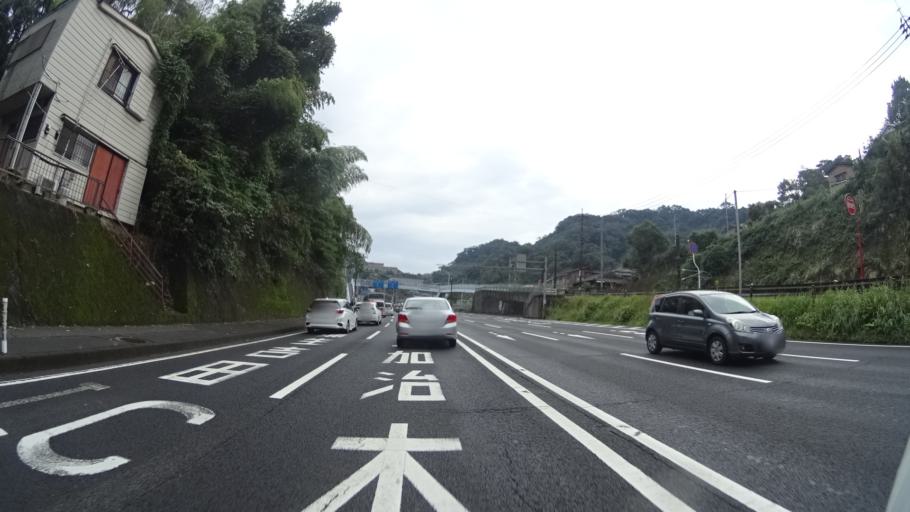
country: JP
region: Kagoshima
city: Kagoshima-shi
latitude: 31.6097
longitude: 130.5696
